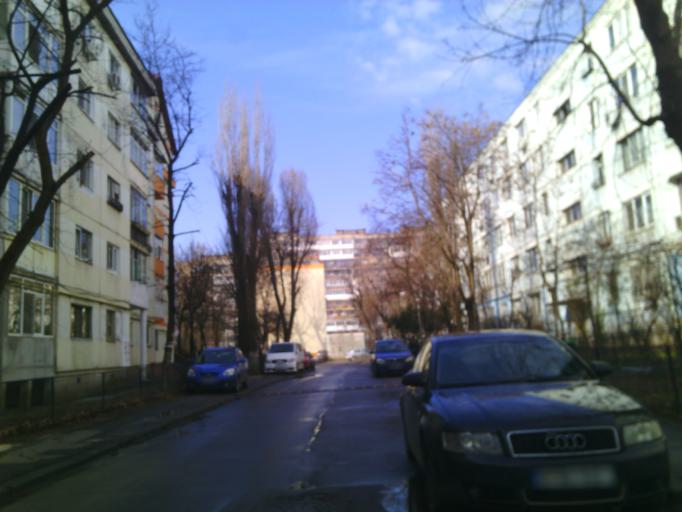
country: RO
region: Bucuresti
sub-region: Municipiul Bucuresti
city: Bucuresti
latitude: 44.3840
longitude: 26.0952
